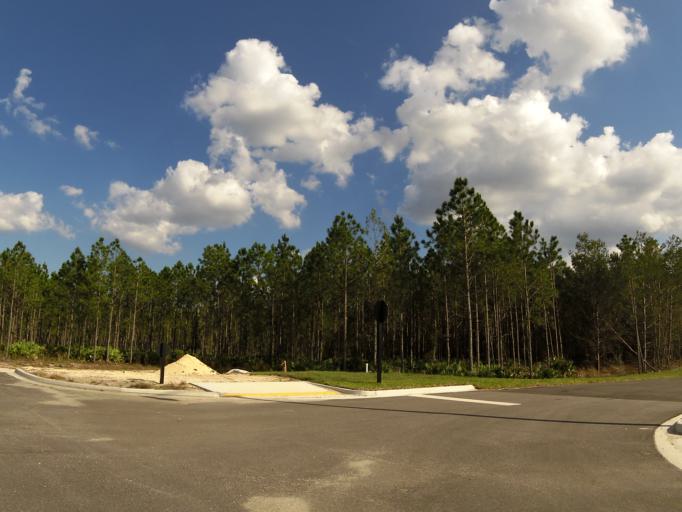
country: US
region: Florida
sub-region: Saint Johns County
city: Palm Valley
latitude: 30.1698
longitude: -81.5053
